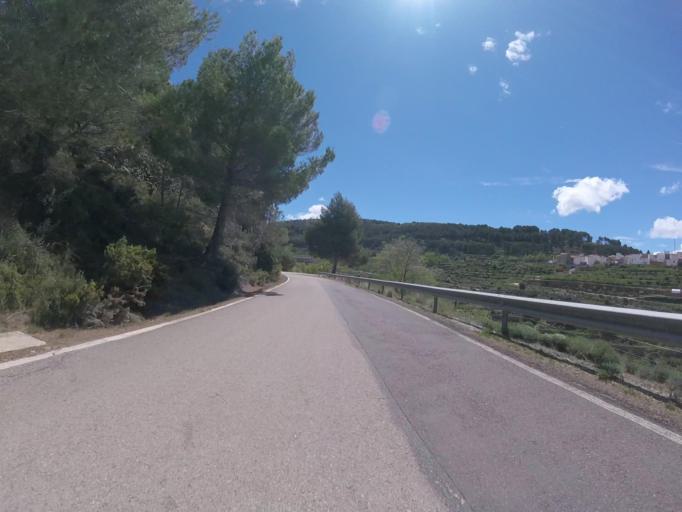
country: ES
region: Valencia
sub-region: Provincia de Castello
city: Sierra-Engarceran
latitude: 40.2733
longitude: -0.0189
